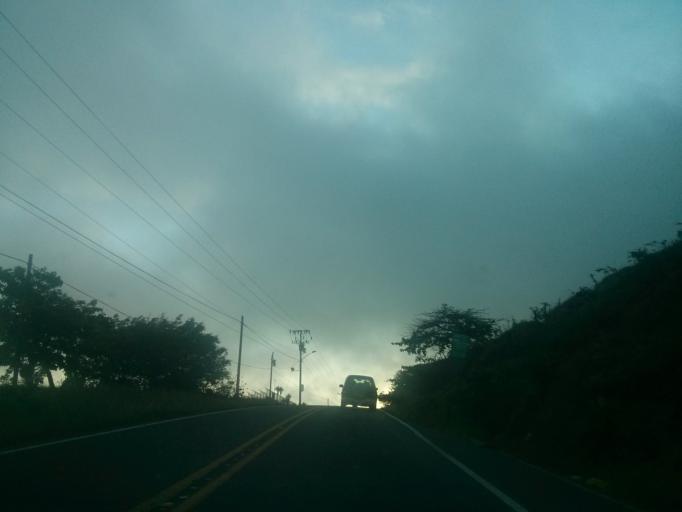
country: CR
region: Cartago
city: Cot
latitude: 9.8867
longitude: -83.8760
